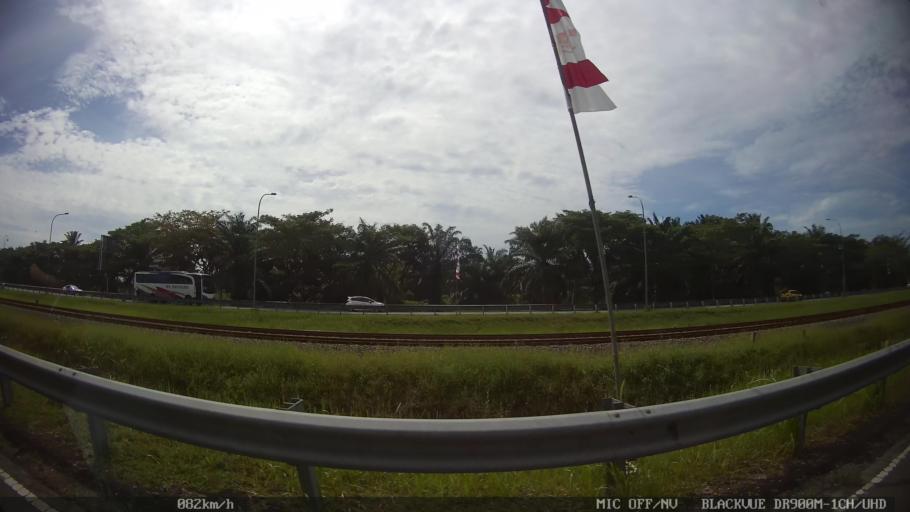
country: ID
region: North Sumatra
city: Percut
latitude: 3.6263
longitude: 98.8696
